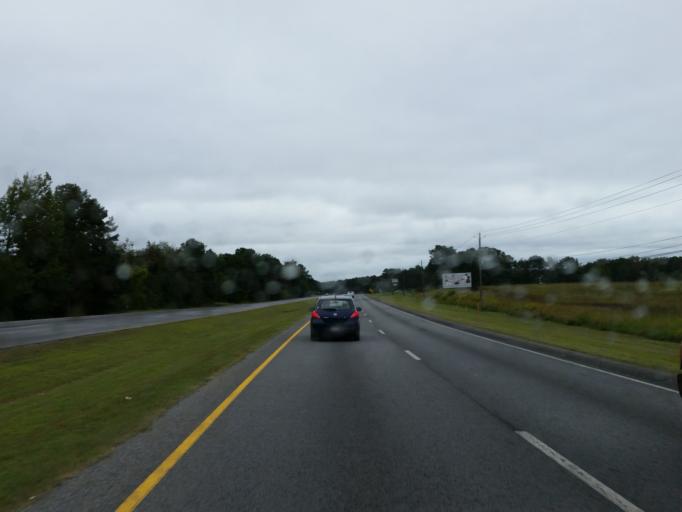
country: US
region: Georgia
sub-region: Clayton County
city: Lovejoy
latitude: 33.4378
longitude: -84.3209
